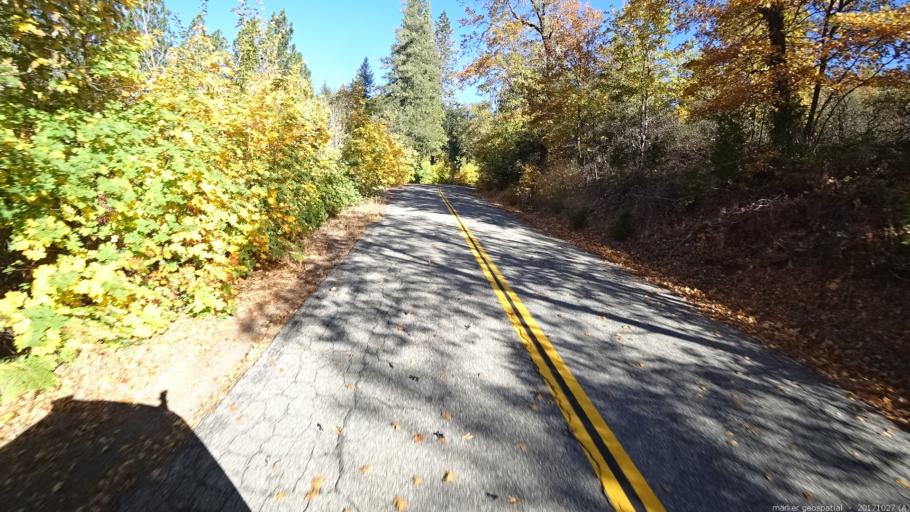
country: US
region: California
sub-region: Shasta County
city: Burney
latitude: 40.8589
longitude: -121.9106
